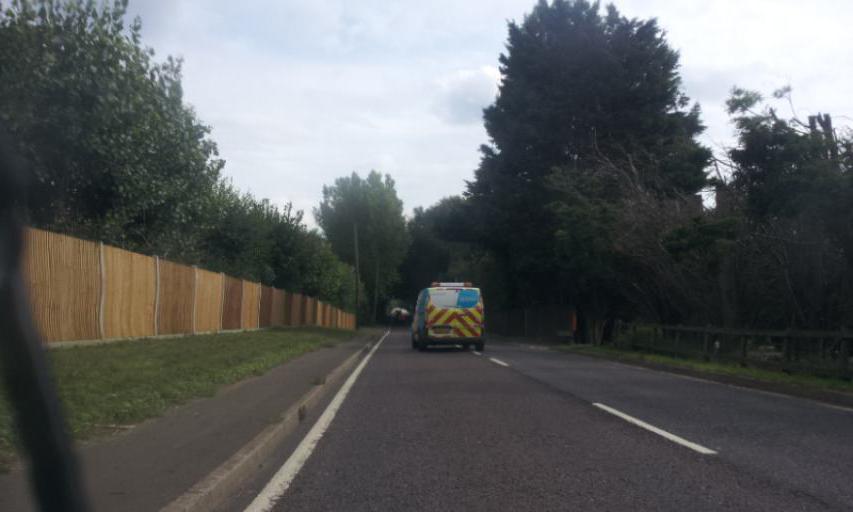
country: GB
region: England
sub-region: Kent
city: Kings Hill
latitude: 51.2604
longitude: 0.3657
